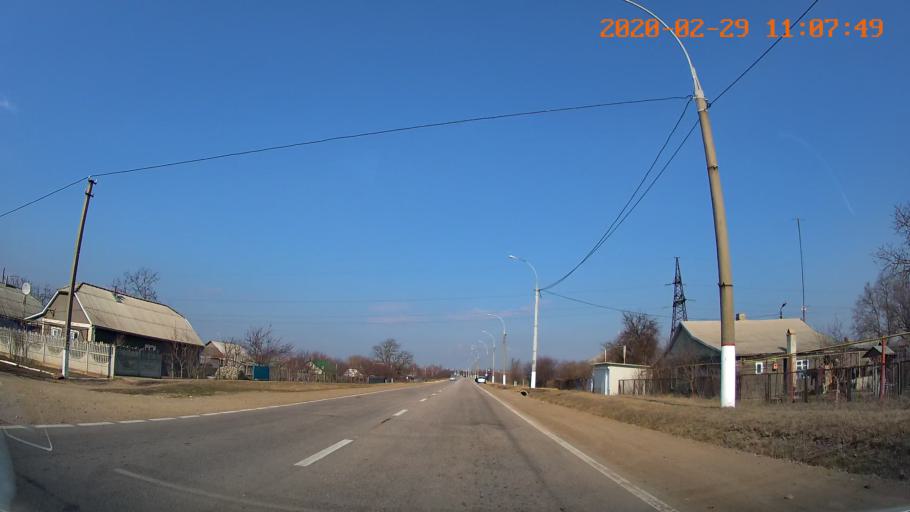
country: MD
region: Criuleni
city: Criuleni
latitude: 47.2285
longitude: 29.1797
